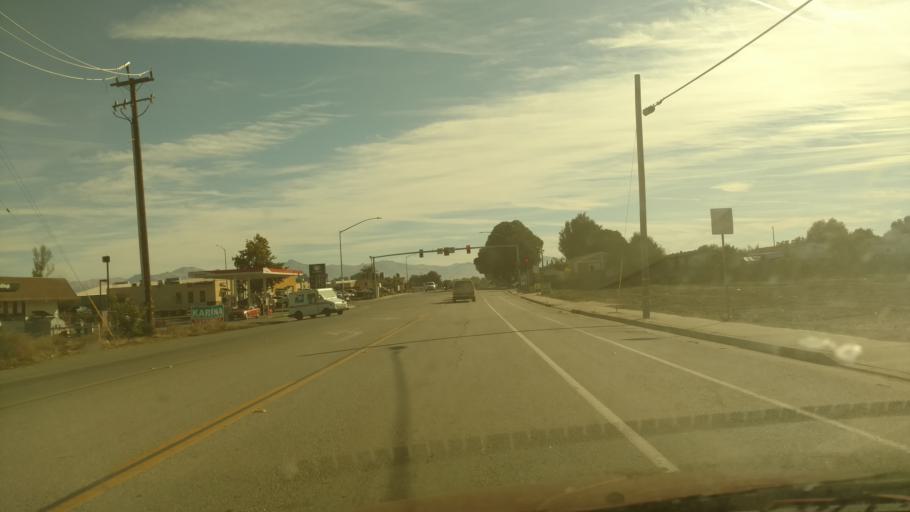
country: US
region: California
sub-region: San Benito County
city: Hollister
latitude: 36.8531
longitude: -121.4224
